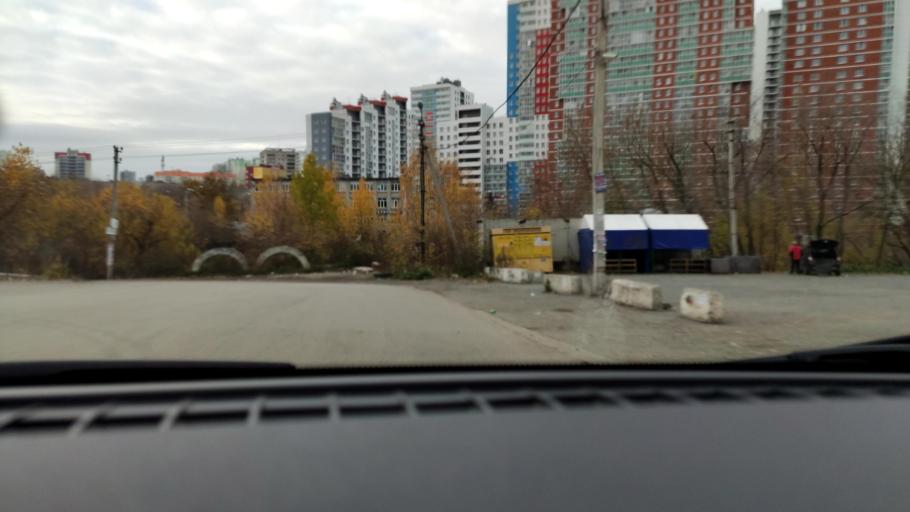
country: RU
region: Perm
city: Perm
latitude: 57.9995
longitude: 56.2231
